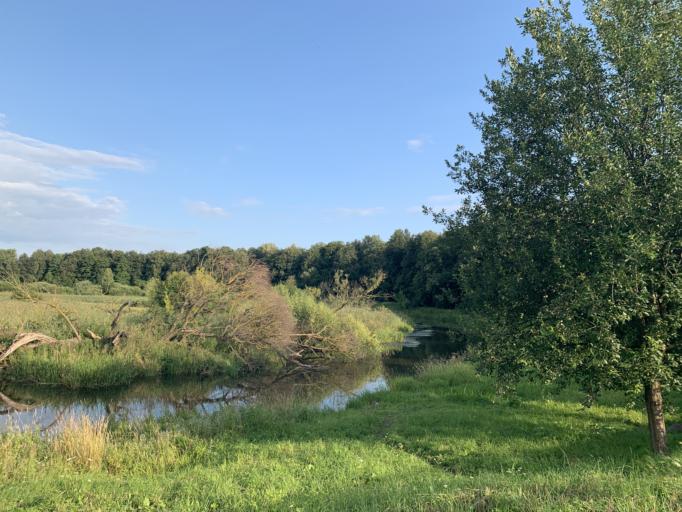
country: BY
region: Minsk
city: Minsk
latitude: 53.8572
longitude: 27.5800
